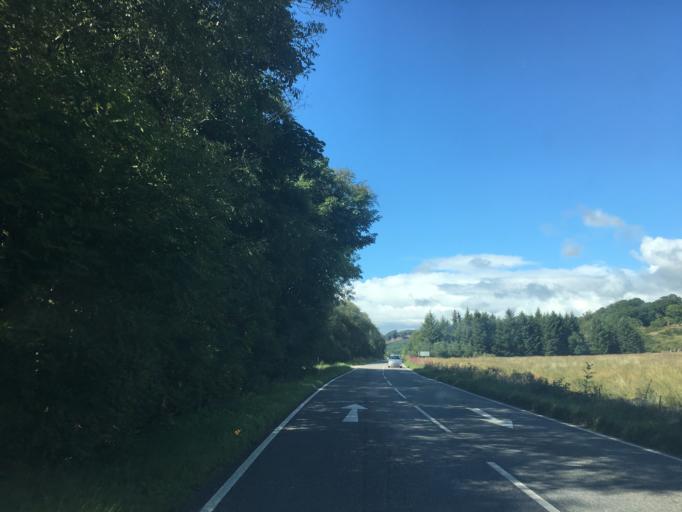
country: GB
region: Scotland
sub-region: Argyll and Bute
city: Lochgilphead
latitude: 56.0931
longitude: -5.4734
